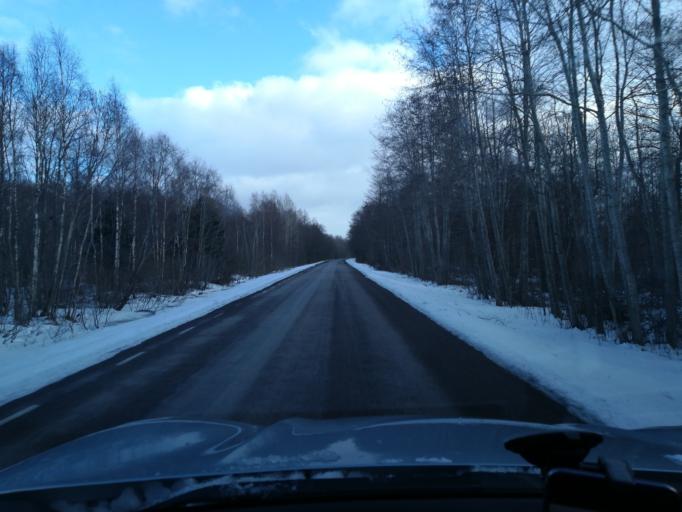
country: EE
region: Harju
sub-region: Keila linn
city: Keila
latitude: 59.4423
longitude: 24.3884
